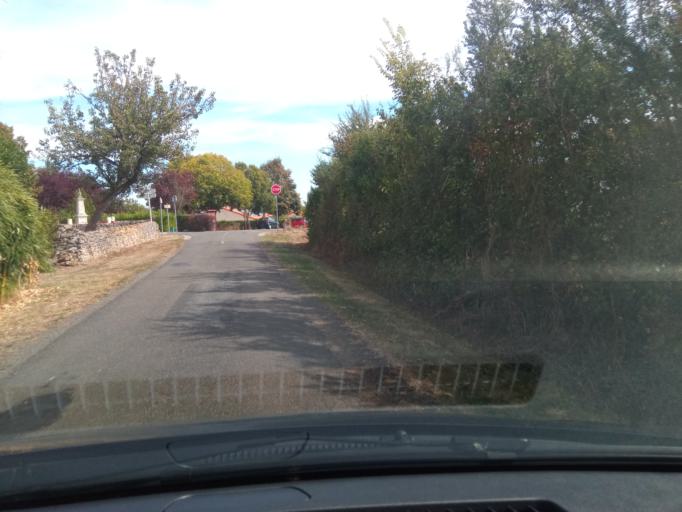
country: FR
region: Poitou-Charentes
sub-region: Departement de la Vienne
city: Chauvigny
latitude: 46.5541
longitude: 0.7448
